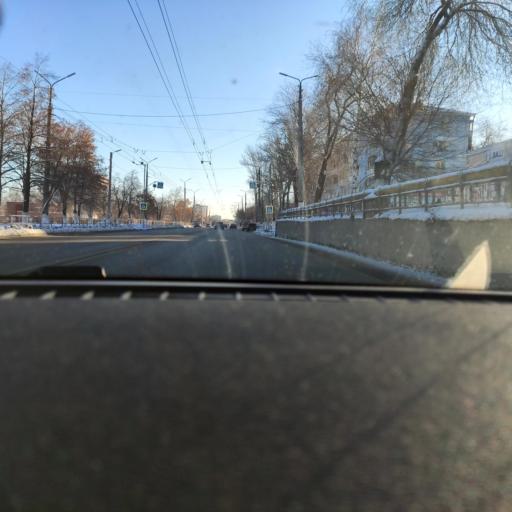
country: RU
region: Samara
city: Novokuybyshevsk
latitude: 53.1002
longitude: 49.9601
